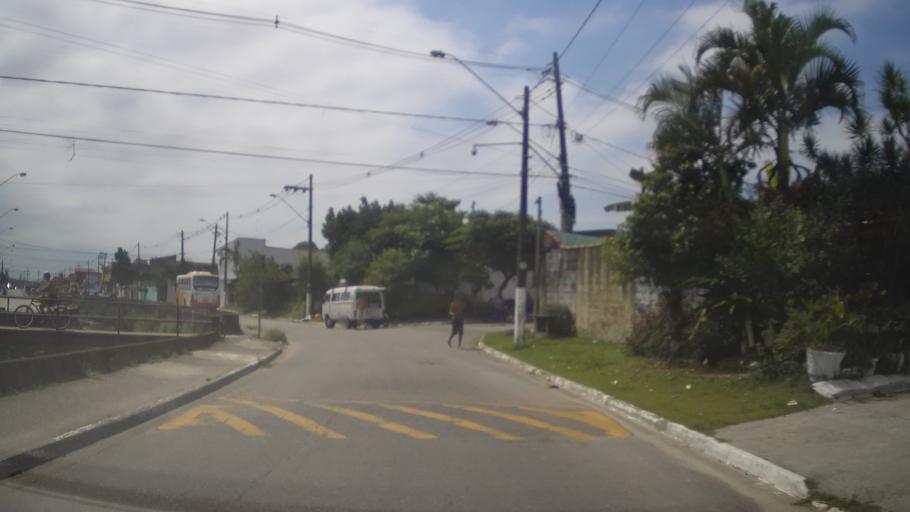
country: BR
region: Sao Paulo
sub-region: Praia Grande
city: Praia Grande
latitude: -24.0216
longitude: -46.4970
